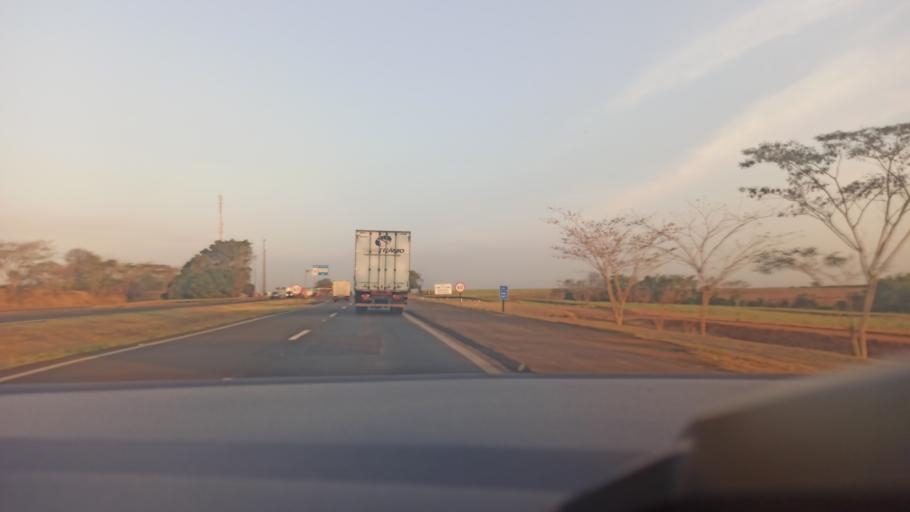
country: BR
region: Sao Paulo
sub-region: Santa Adelia
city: Santa Adelia
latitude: -21.3806
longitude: -48.7358
